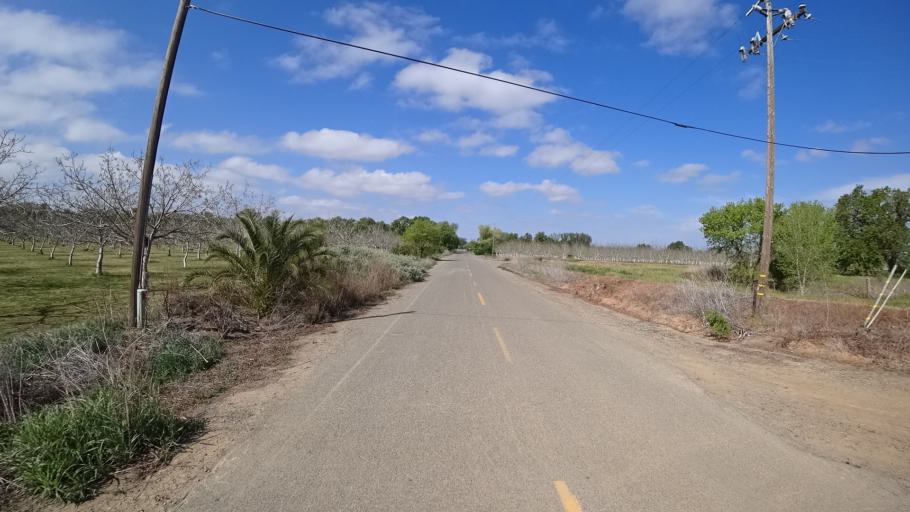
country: US
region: California
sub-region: Colusa County
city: Colusa
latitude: 39.4199
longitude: -121.9586
